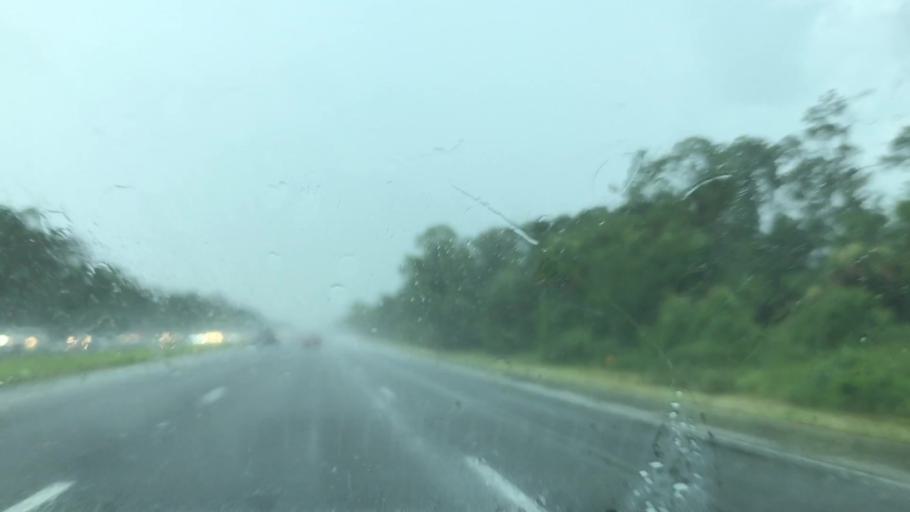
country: US
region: Florida
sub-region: Flagler County
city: Flagler Beach
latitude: 29.3932
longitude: -81.1507
